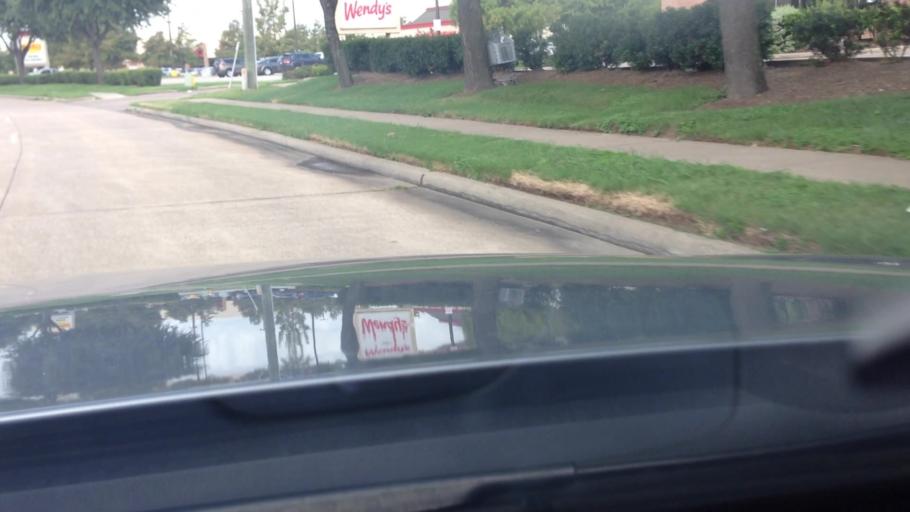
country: US
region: Texas
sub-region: Harris County
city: Hudson
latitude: 29.9556
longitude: -95.5449
